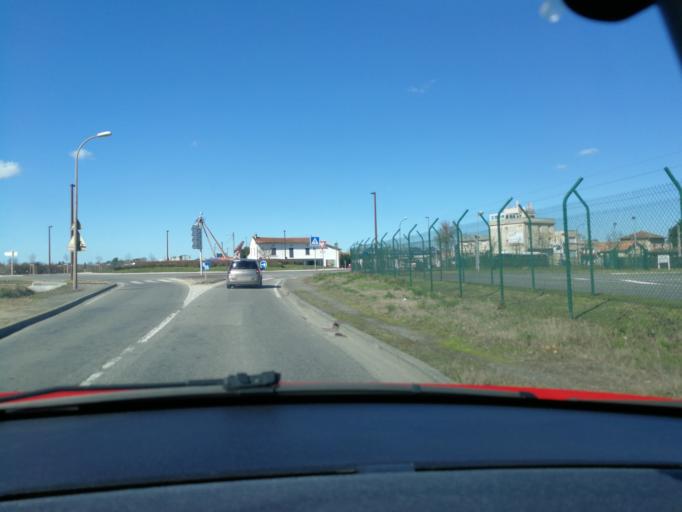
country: FR
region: Midi-Pyrenees
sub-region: Departement de la Haute-Garonne
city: Portet-sur-Garonne
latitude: 43.5450
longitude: 1.3875
